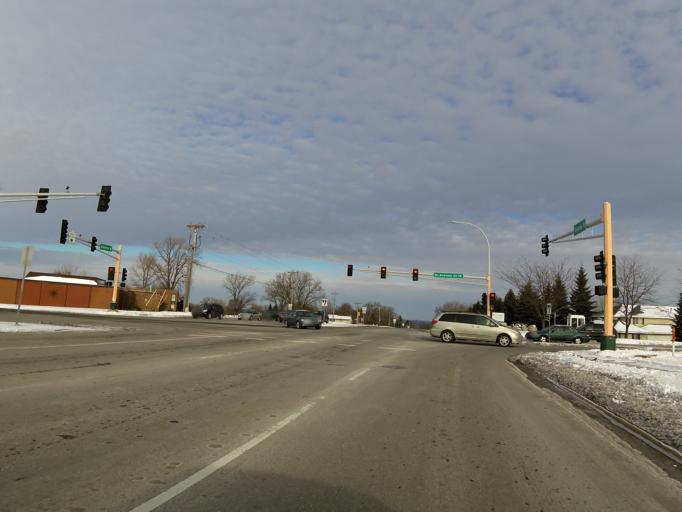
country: US
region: Minnesota
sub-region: Dakota County
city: Burnsville
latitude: 44.7480
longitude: -93.3029
